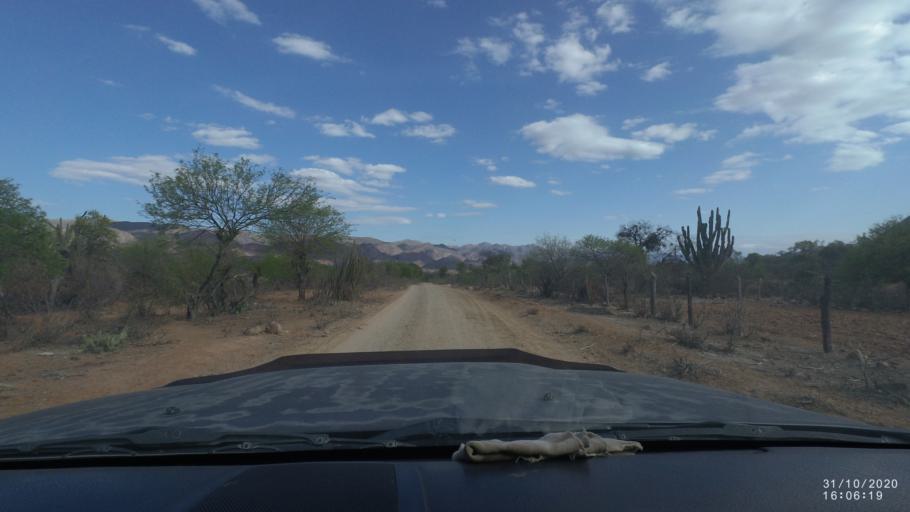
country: BO
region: Chuquisaca
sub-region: Provincia Zudanez
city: Mojocoya
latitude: -18.3725
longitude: -64.6478
